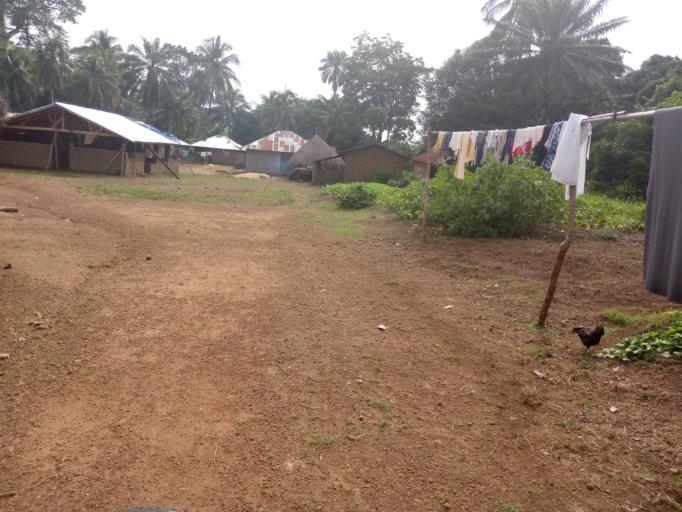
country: SL
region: Eastern Province
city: Buedu
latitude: 8.4521
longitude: -10.3380
